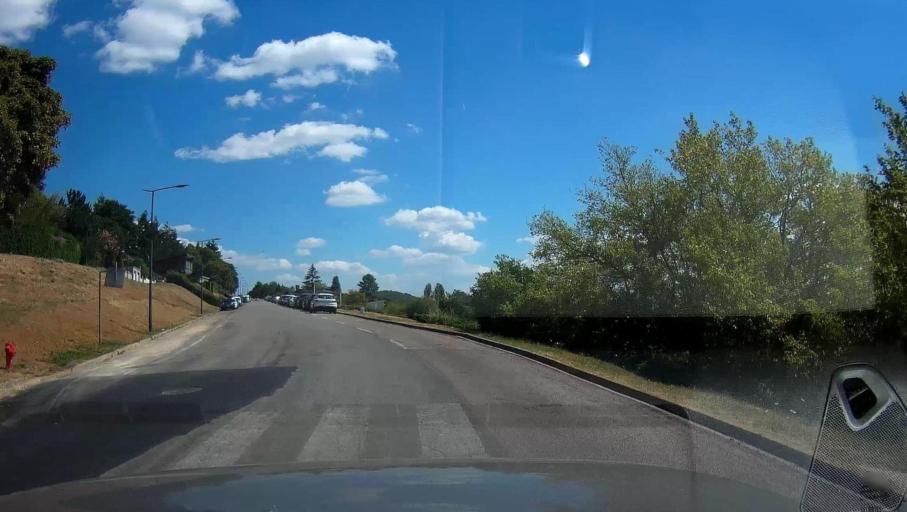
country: FR
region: Champagne-Ardenne
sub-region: Departement de la Haute-Marne
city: Langres
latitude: 47.8691
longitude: 5.3760
